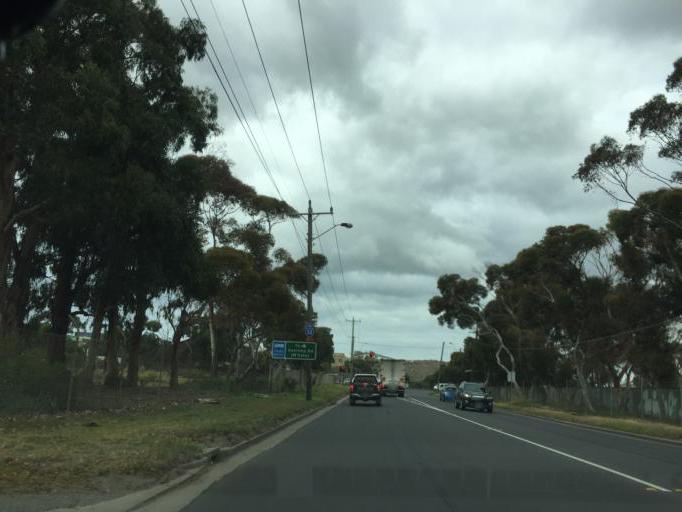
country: AU
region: Victoria
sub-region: Brimbank
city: Brooklyn
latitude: -37.8066
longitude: 144.8380
